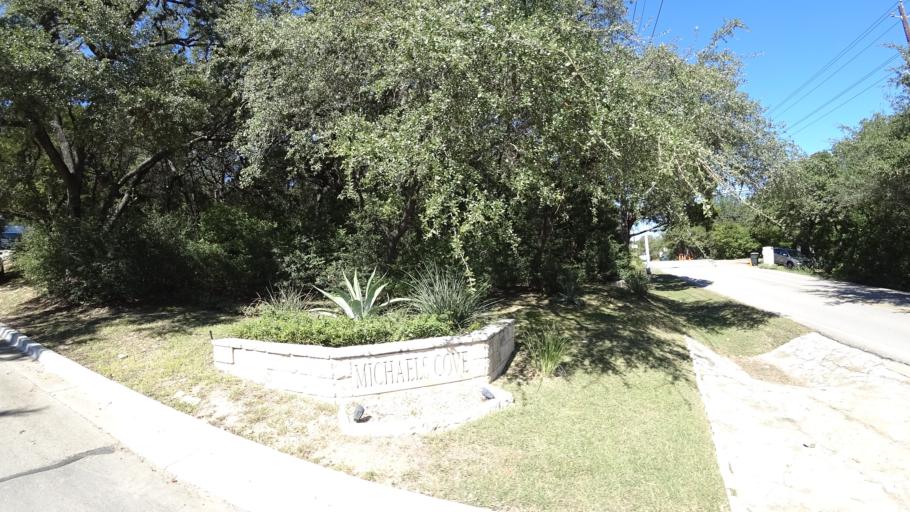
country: US
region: Texas
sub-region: Travis County
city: West Lake Hills
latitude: 30.3225
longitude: -97.7794
